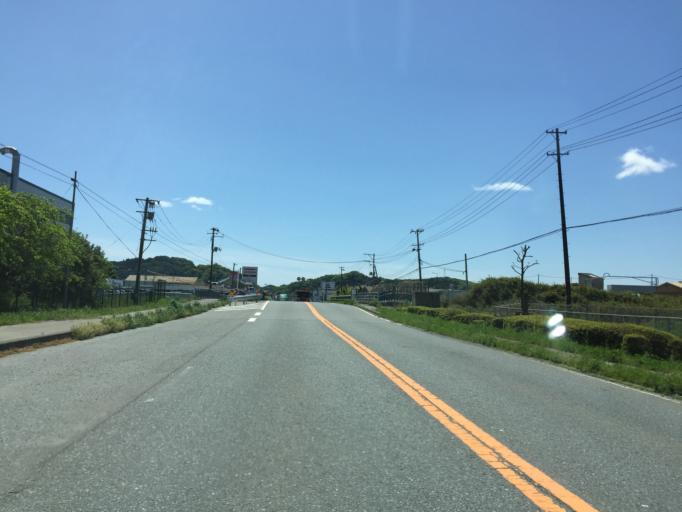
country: JP
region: Fukushima
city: Iwaki
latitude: 36.9828
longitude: 140.8699
